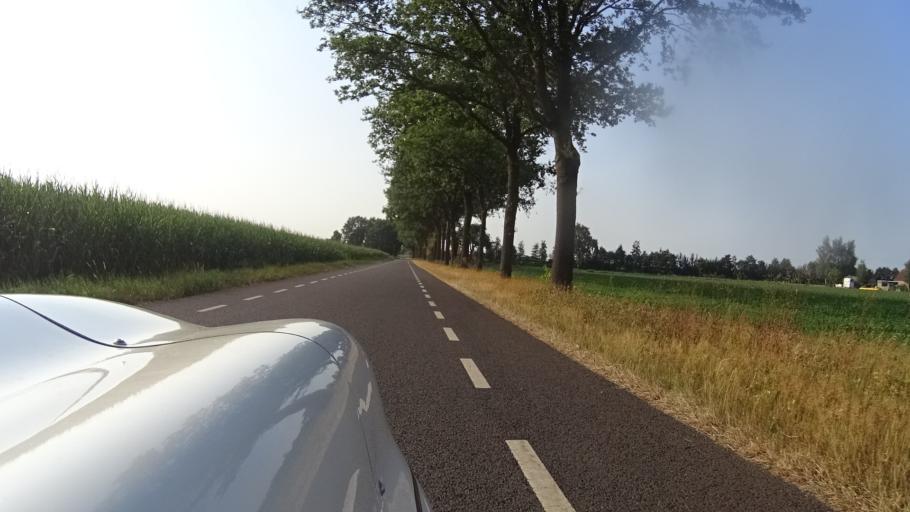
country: NL
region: North Brabant
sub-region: Gemeente Uden
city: Odiliapeel
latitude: 51.6799
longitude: 5.7264
